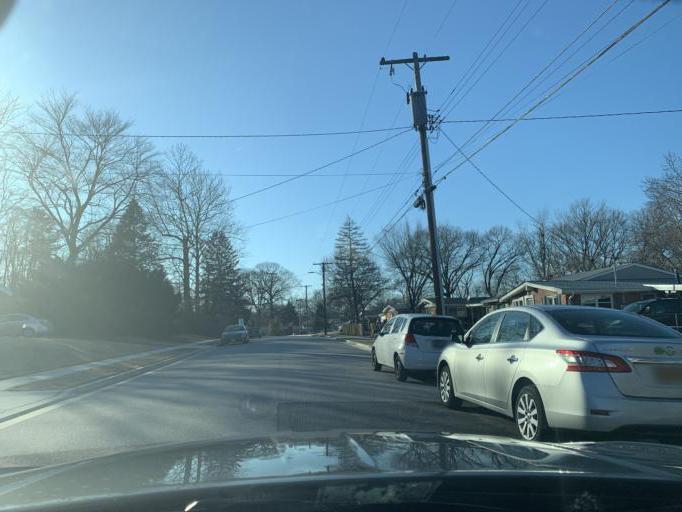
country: US
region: Maryland
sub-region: Anne Arundel County
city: Glen Burnie
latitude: 39.1473
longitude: -76.6265
